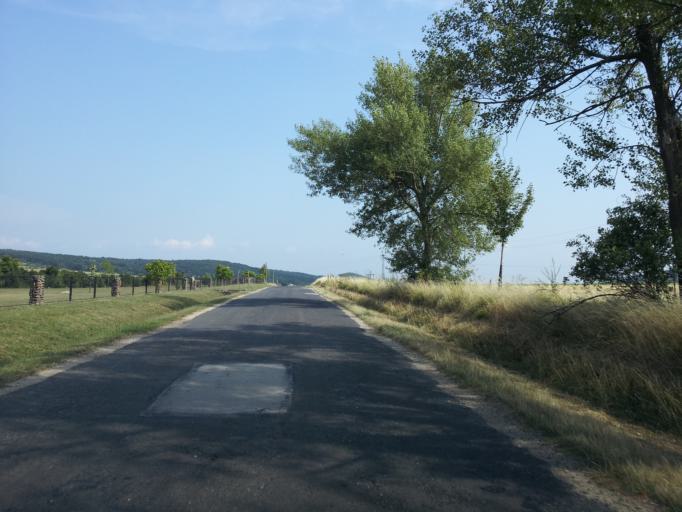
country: HU
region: Veszprem
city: Nemesvamos
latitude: 47.0111
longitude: 17.8178
